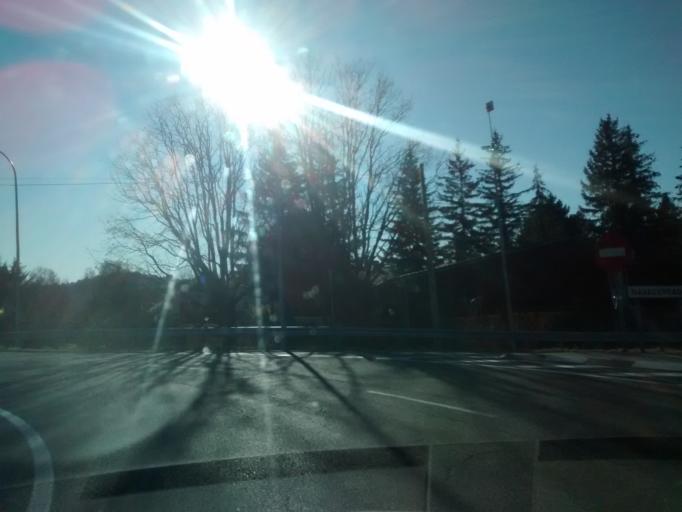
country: ES
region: Madrid
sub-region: Provincia de Madrid
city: Navacerrada
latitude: 40.7335
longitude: -4.0068
